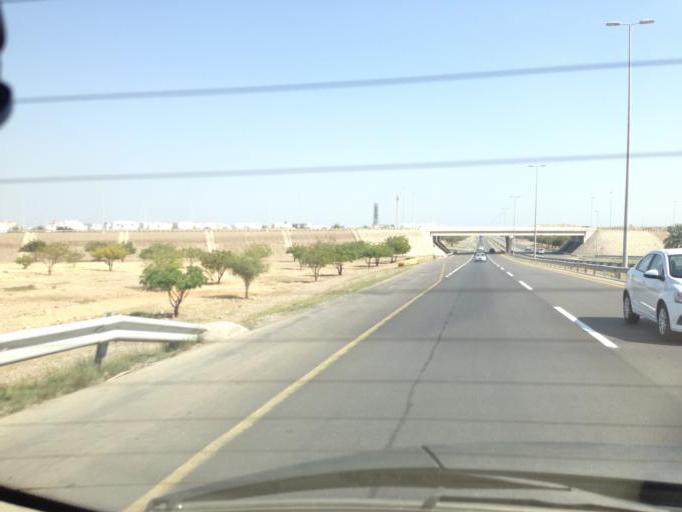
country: OM
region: Muhafazat Masqat
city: As Sib al Jadidah
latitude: 23.5716
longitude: 58.1915
